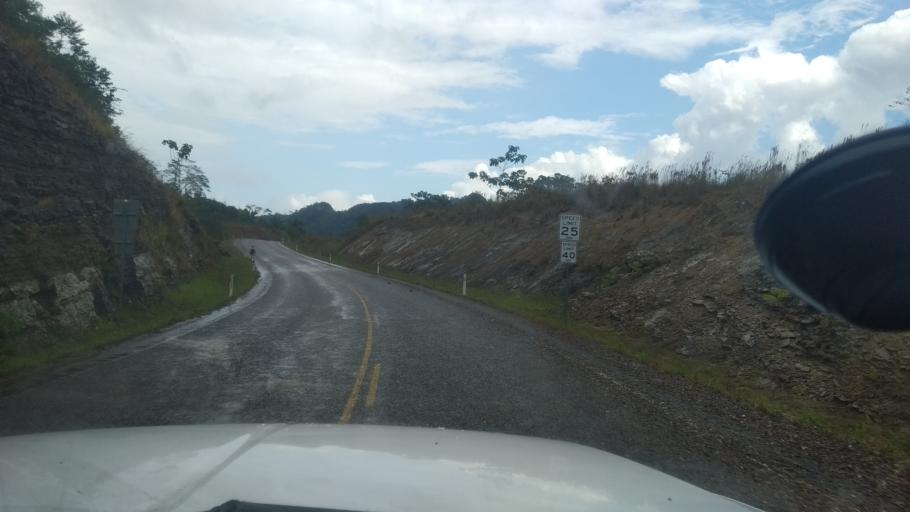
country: GT
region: Peten
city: San Luis
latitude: 16.1841
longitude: -89.2041
